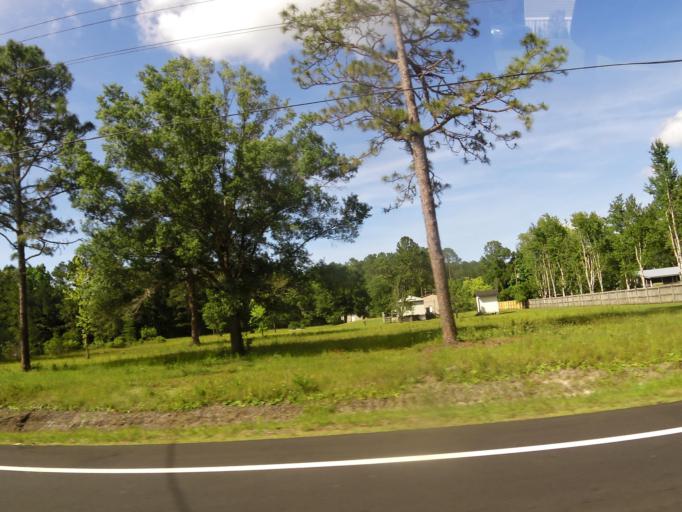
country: US
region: Florida
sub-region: Nassau County
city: Callahan
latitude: 30.5857
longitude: -81.8569
